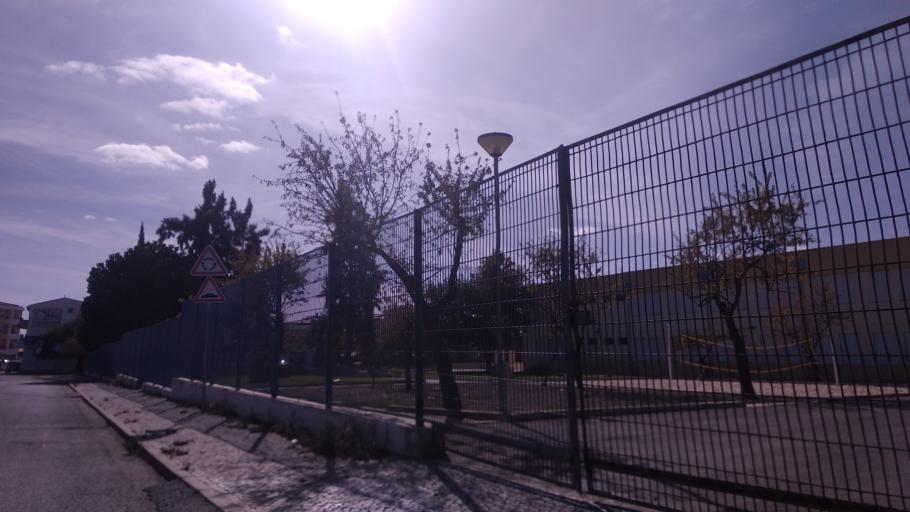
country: PT
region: Faro
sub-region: Sao Bras de Alportel
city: Sao Bras de Alportel
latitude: 37.1578
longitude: -7.8855
